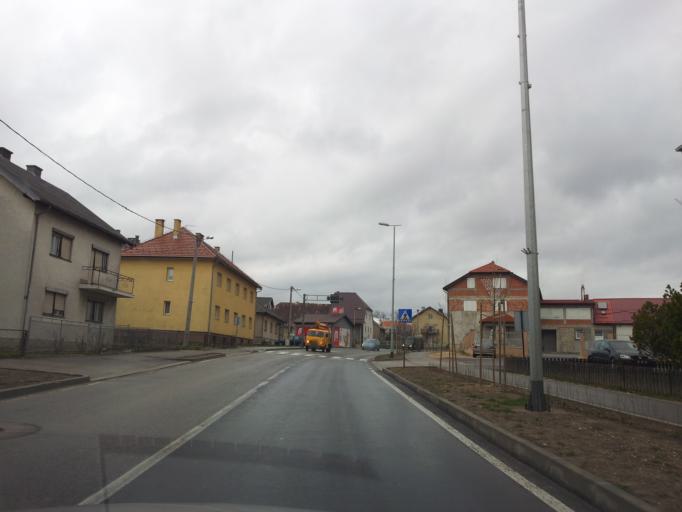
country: BA
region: Federation of Bosnia and Herzegovina
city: Izacic
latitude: 44.7462
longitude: 15.7046
